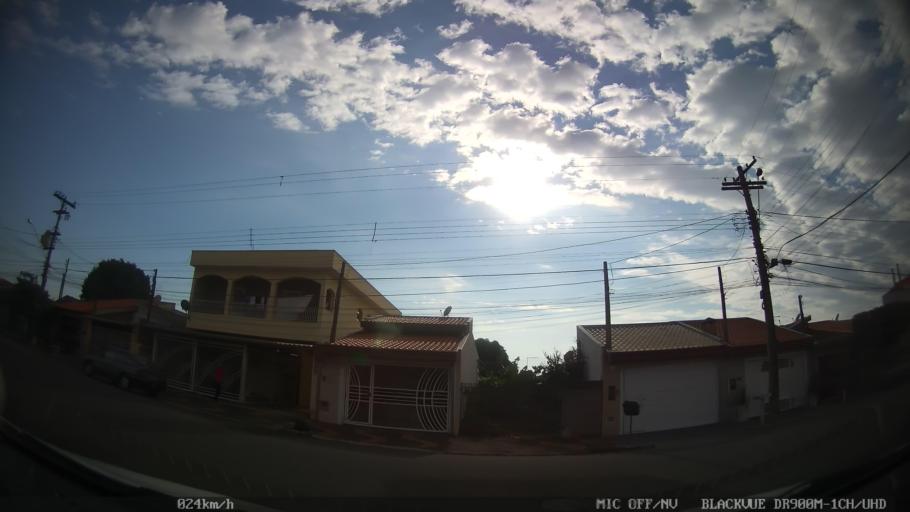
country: BR
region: Sao Paulo
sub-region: Americana
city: Americana
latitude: -22.7215
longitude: -47.3690
